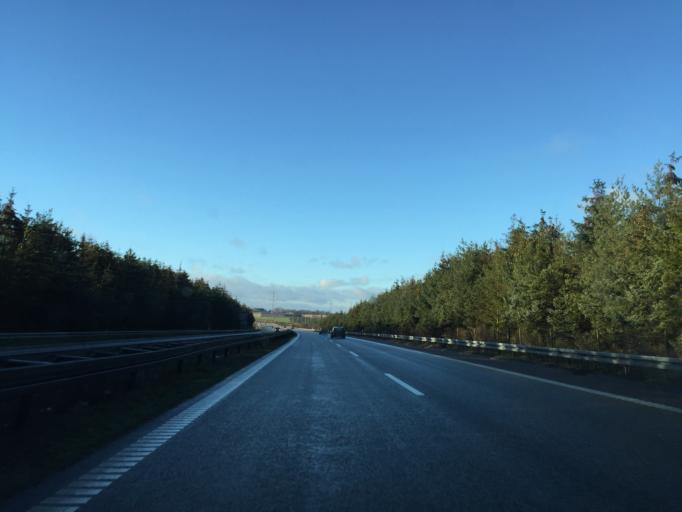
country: DK
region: Zealand
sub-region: Ringsted Kommune
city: Ringsted
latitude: 55.4576
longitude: 11.7680
